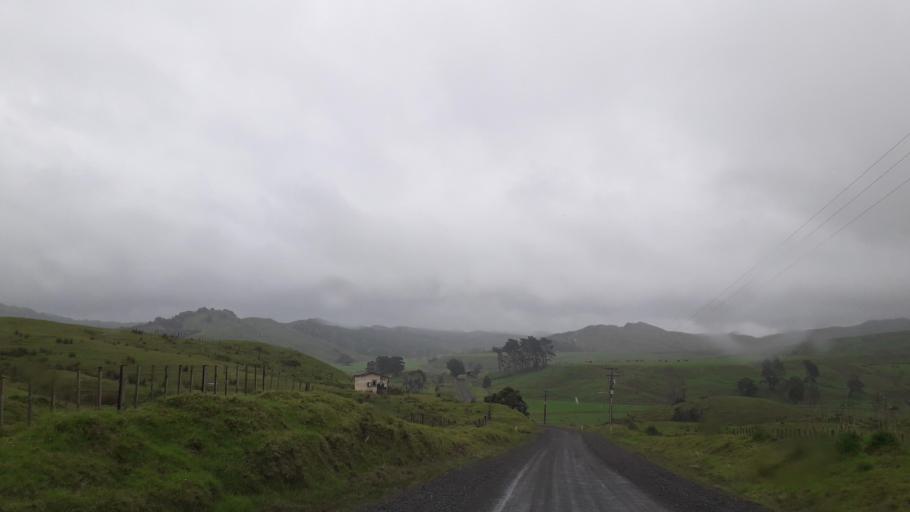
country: NZ
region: Northland
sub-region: Far North District
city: Kaitaia
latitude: -35.4144
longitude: 173.3661
